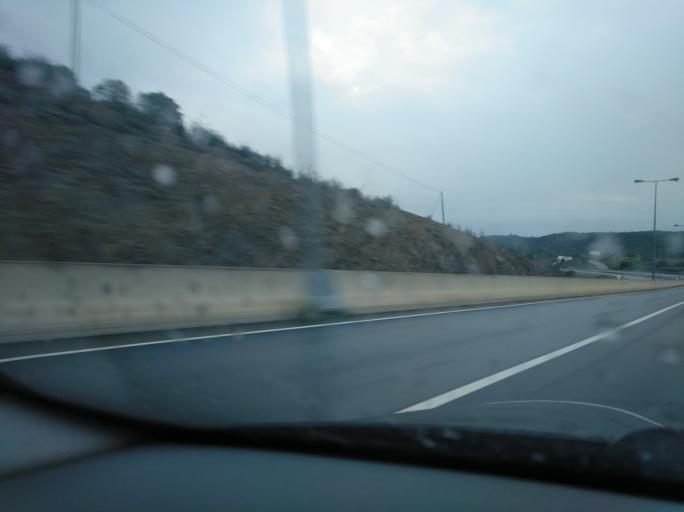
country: PT
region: Faro
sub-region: Castro Marim
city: Castro Marim
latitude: 37.3363
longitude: -7.4974
